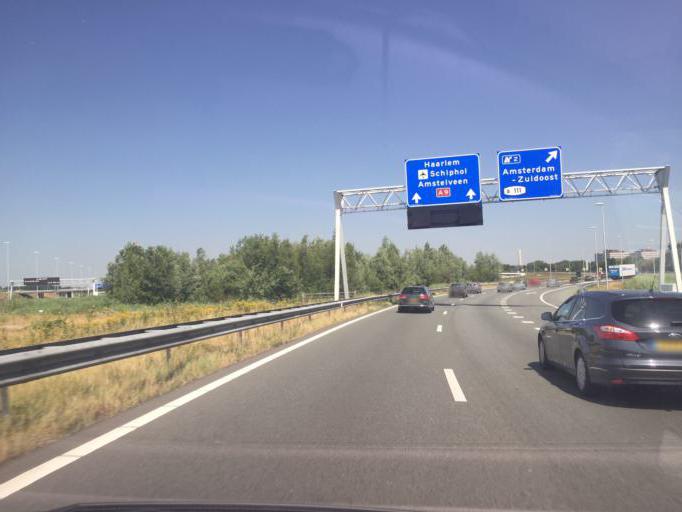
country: NL
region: North Holland
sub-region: Gemeente Amsterdam
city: Amsterdam-Zuidoost
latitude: 52.2823
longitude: 4.9521
